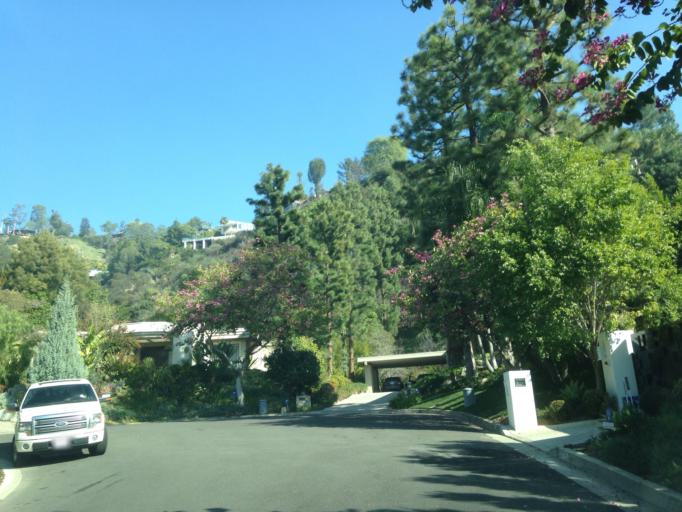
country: US
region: California
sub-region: Los Angeles County
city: Beverly Hills
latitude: 34.1023
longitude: -118.3928
